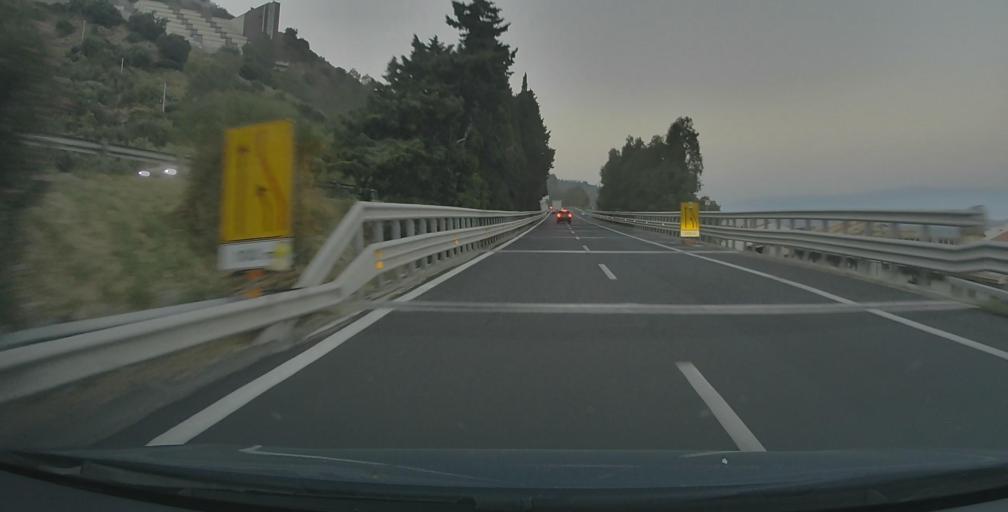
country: IT
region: Sicily
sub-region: Messina
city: Guidomandri Marina
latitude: 38.0334
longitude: 15.4484
